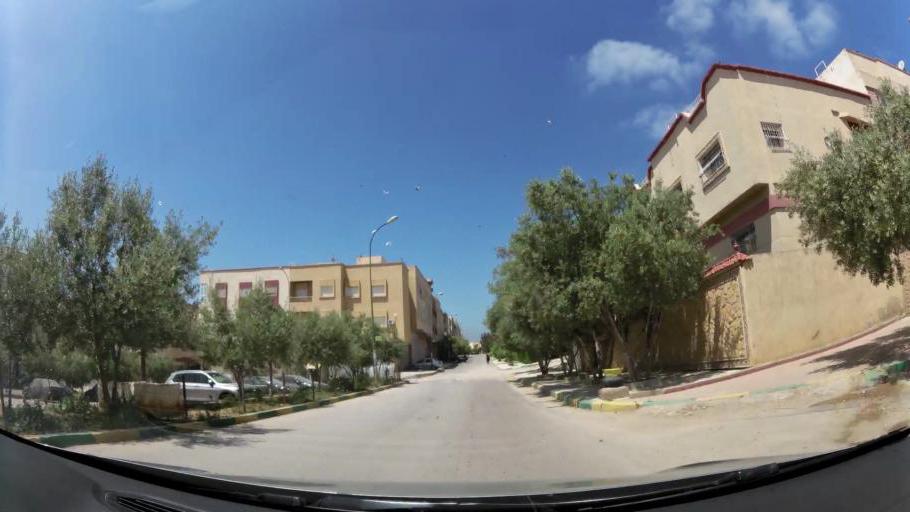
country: MA
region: Fes-Boulemane
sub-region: Fes
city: Fes
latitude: 34.0619
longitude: -5.0285
